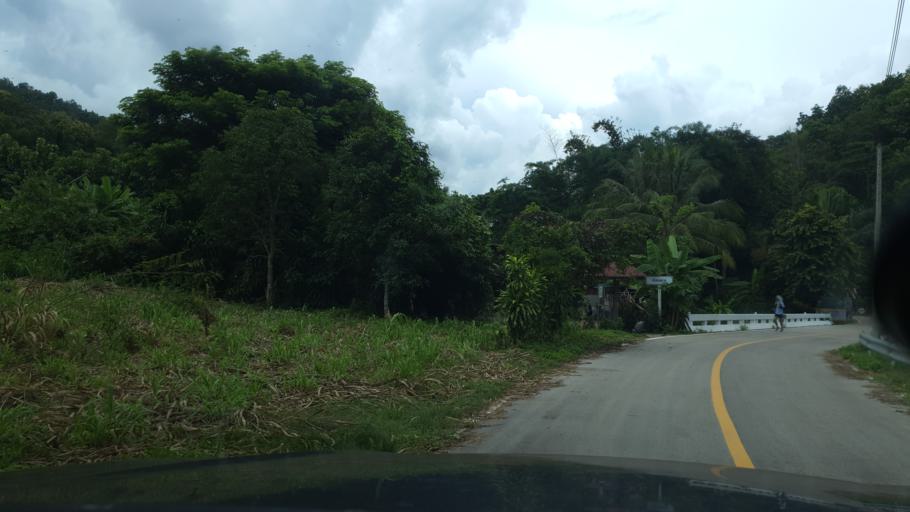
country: TH
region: Lamphun
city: Mae Tha
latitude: 18.4369
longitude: 99.2683
